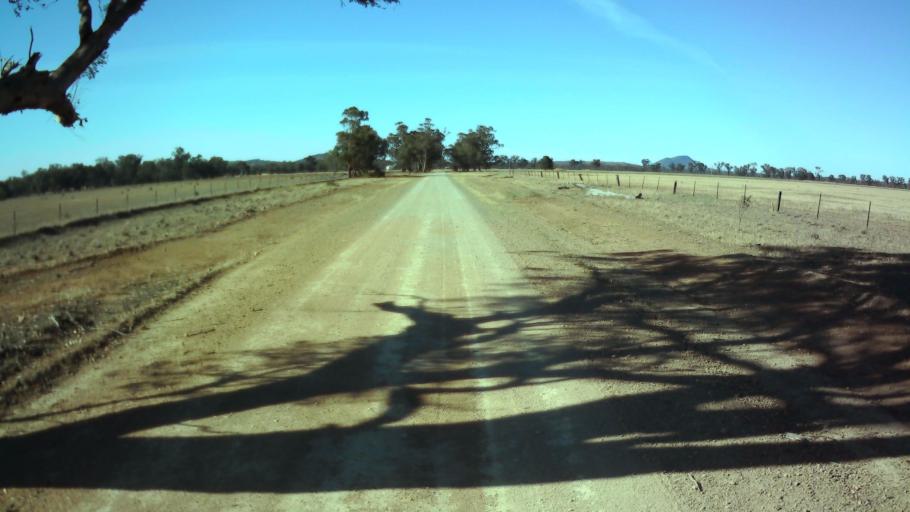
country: AU
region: New South Wales
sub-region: Weddin
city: Grenfell
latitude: -33.8438
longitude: 147.8767
